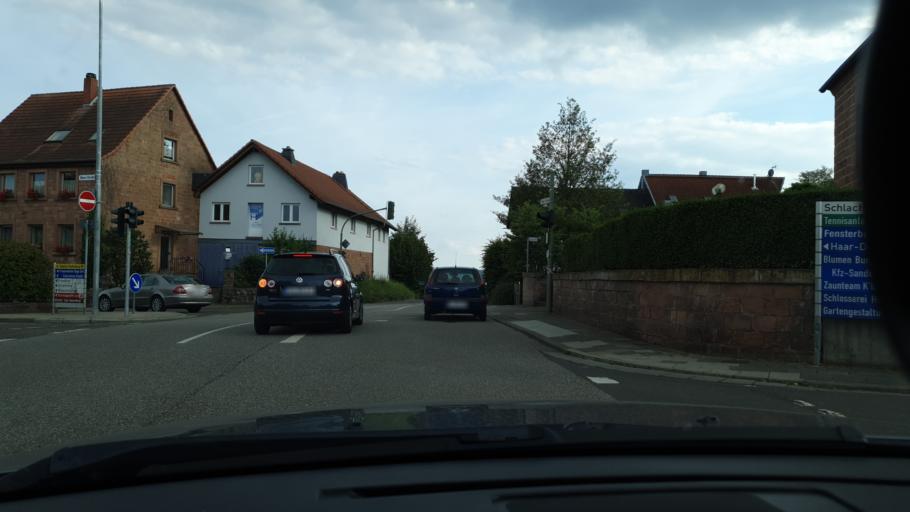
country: DE
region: Rheinland-Pfalz
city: Otterbach
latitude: 49.4693
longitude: 7.7619
